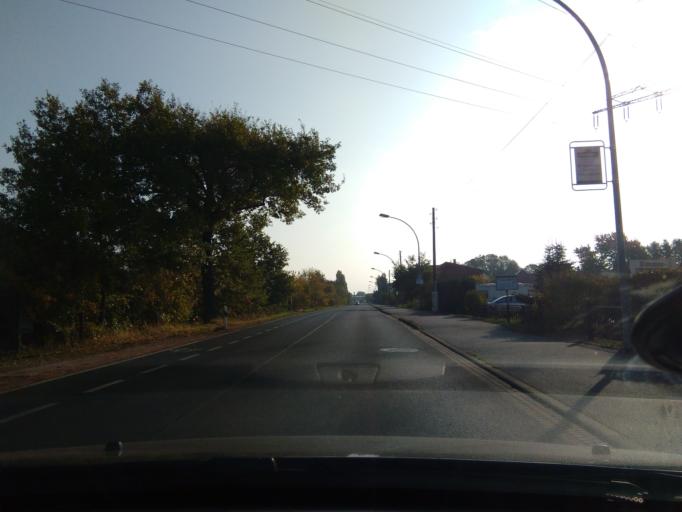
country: DE
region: Saxony
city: Coswig
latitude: 51.1286
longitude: 13.5520
